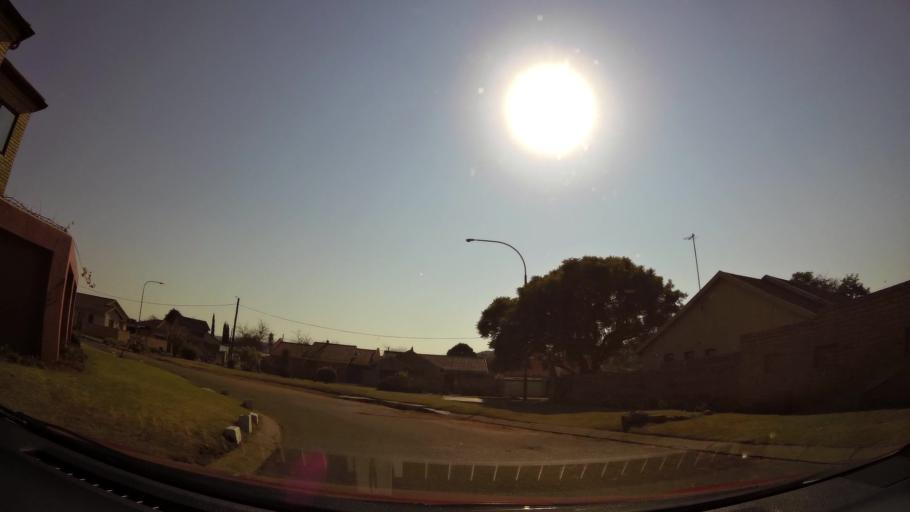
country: ZA
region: Gauteng
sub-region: City of Johannesburg Metropolitan Municipality
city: Johannesburg
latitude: -26.2468
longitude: 27.9596
